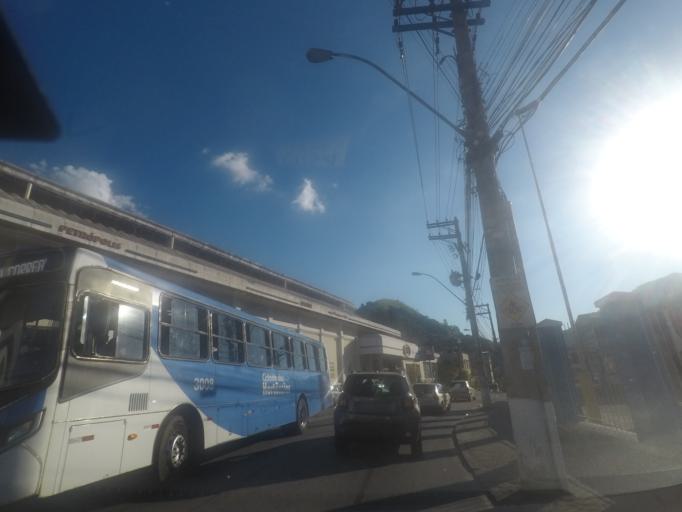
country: BR
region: Rio de Janeiro
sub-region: Petropolis
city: Petropolis
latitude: -22.4869
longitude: -43.1512
